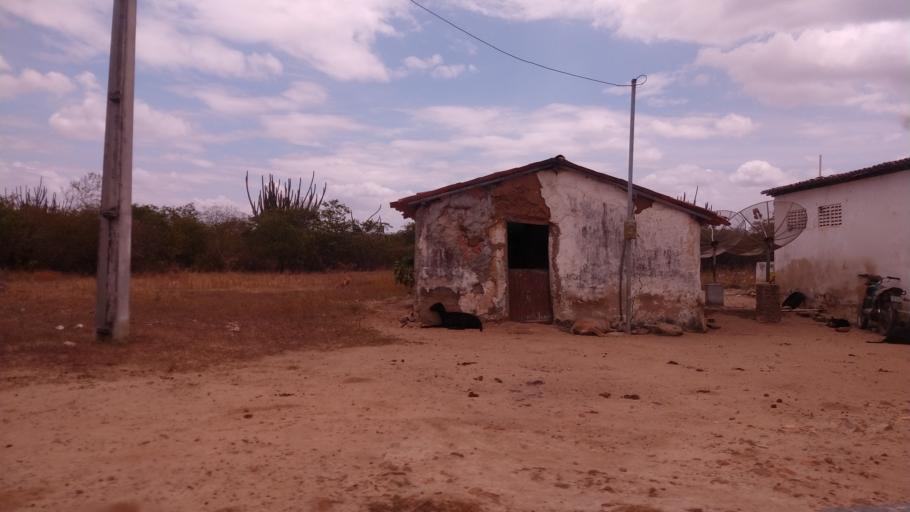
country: BR
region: Rio Grande do Norte
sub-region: Sao Paulo Do Potengi
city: Sao Paulo do Potengi
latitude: -5.9285
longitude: -35.9054
